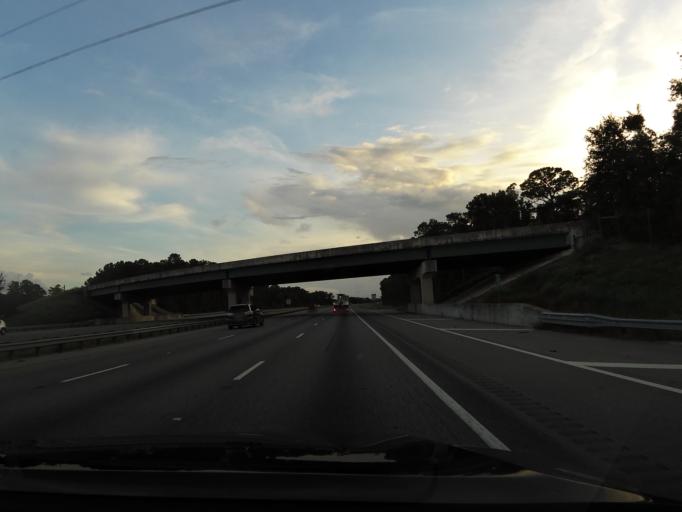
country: US
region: Georgia
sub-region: Glynn County
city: Dock Junction
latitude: 31.1858
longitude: -81.5431
